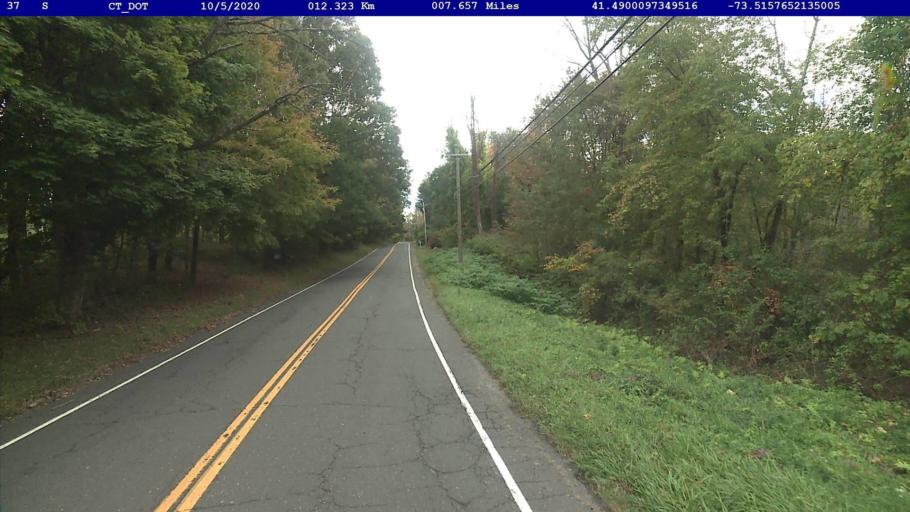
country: US
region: New York
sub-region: Putnam County
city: Putnam Lake
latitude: 41.4900
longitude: -73.5158
